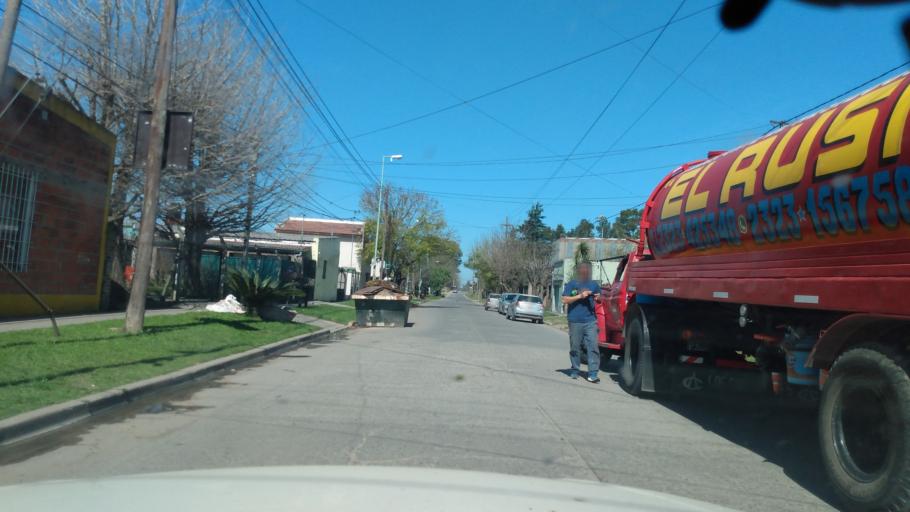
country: AR
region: Buenos Aires
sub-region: Partido de Lujan
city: Lujan
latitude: -34.5810
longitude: -59.1222
